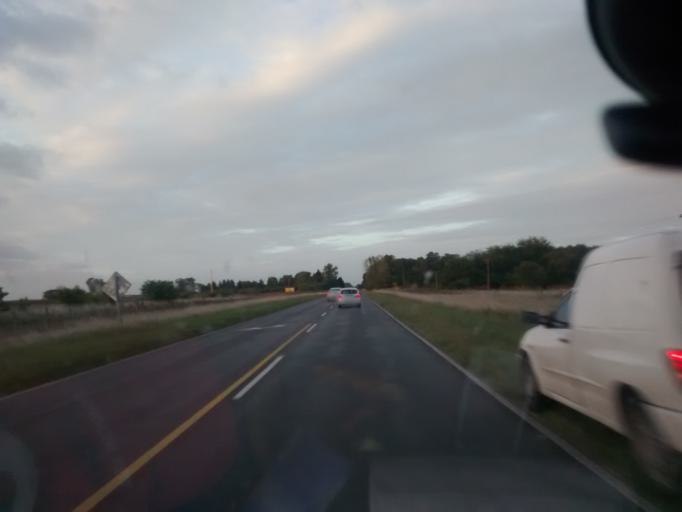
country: AR
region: Buenos Aires
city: Ranchos
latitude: -35.4477
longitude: -58.3179
